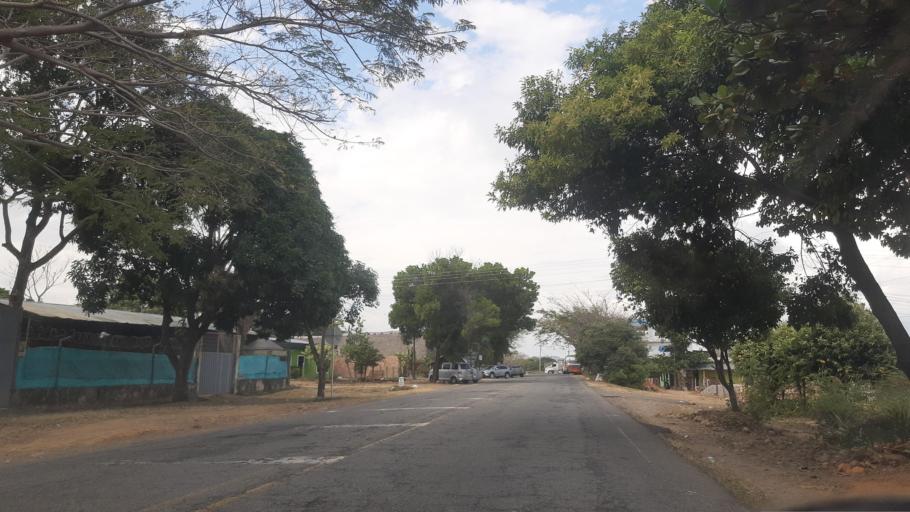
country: CO
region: Casanare
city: Pore
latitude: 5.8839
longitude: -71.9013
